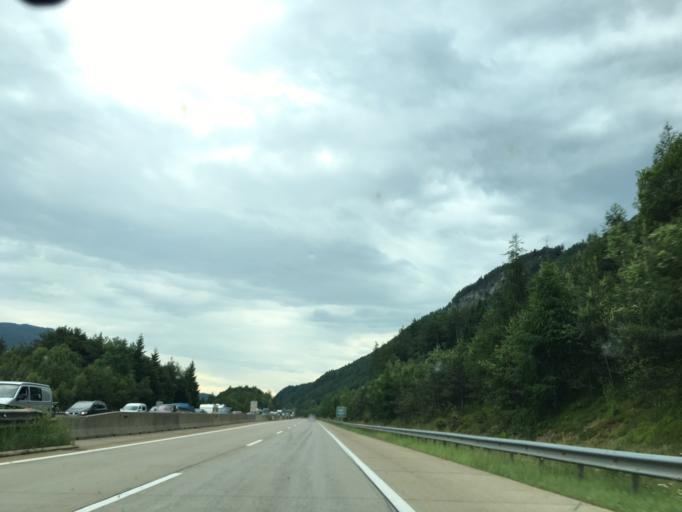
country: AT
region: Carinthia
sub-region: Politischer Bezirk Villach Land
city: Fresach
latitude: 46.6507
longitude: 13.7492
